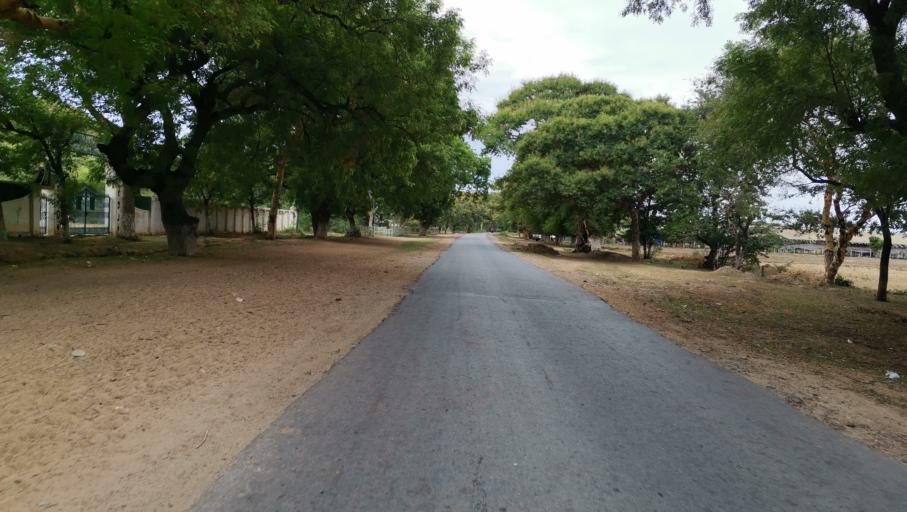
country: MM
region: Mandalay
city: Myingyan
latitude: 21.8483
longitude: 95.4299
